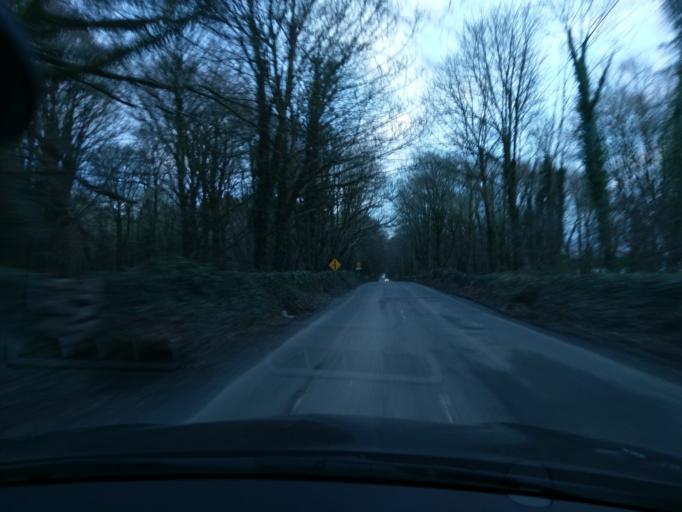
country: IE
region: Connaught
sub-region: County Galway
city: Athenry
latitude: 53.3375
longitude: -8.7721
